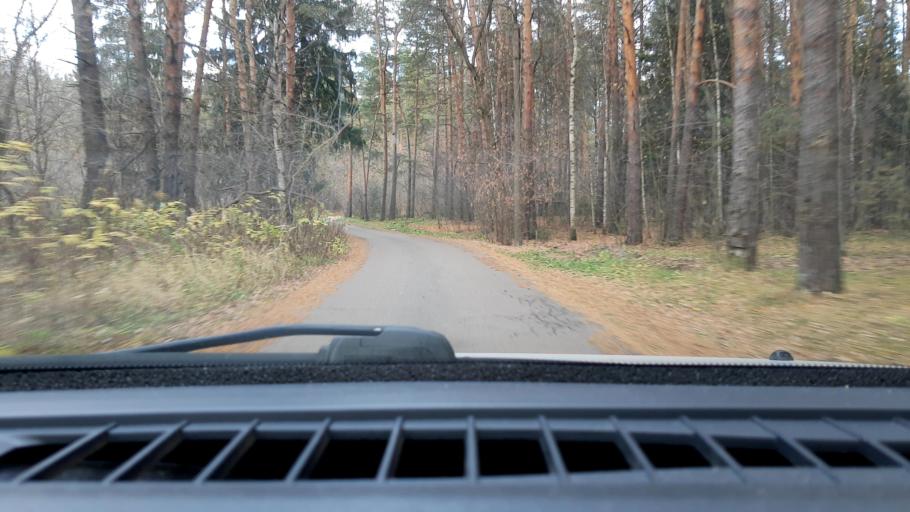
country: RU
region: Nizjnij Novgorod
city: Kstovo
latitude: 56.1691
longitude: 44.1237
